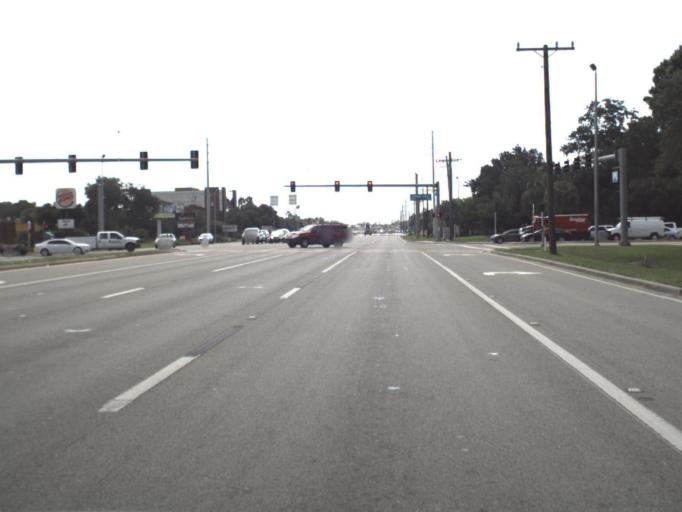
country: US
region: Florida
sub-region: Charlotte County
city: Port Charlotte
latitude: 27.0108
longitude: -82.1419
